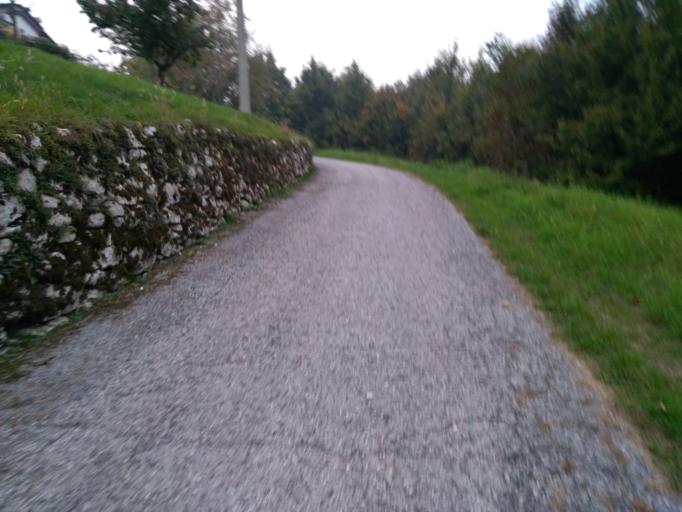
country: IT
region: Veneto
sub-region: Provincia di Vicenza
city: Monte di Malo
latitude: 45.6572
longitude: 11.3585
